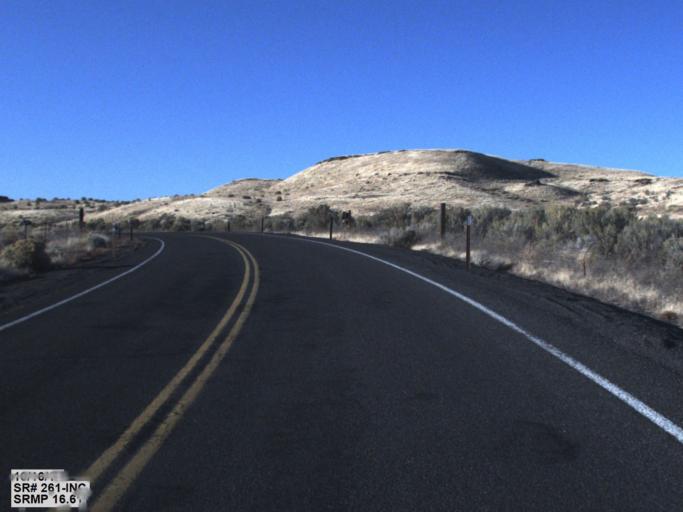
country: US
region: Washington
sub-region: Walla Walla County
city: Waitsburg
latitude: 46.6100
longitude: -118.2224
